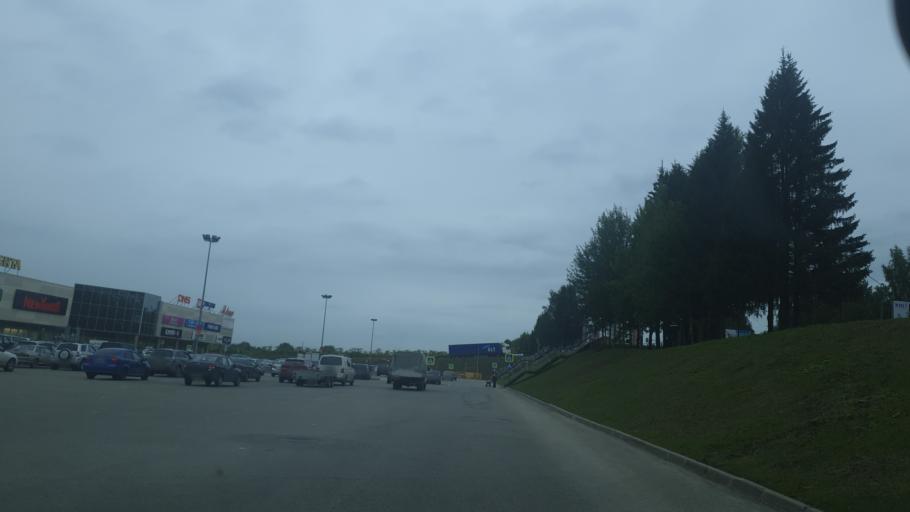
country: RU
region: Komi Republic
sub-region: Syktyvdinskiy Rayon
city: Syktyvkar
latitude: 61.6980
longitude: 50.8046
